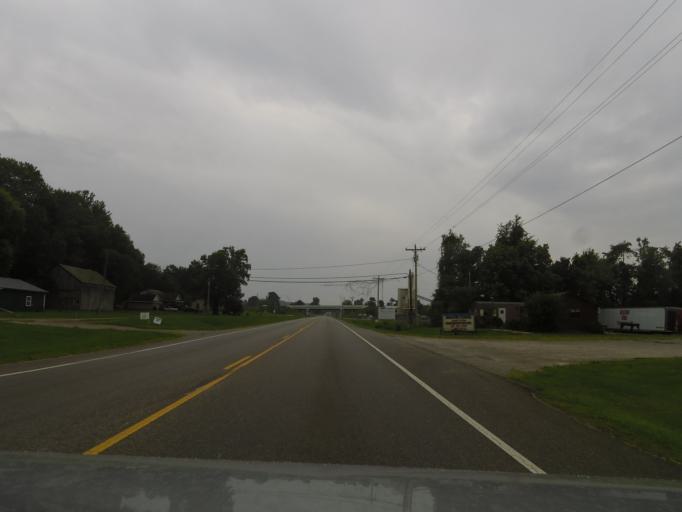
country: US
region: Ohio
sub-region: Brown County
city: Aberdeen
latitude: 38.6895
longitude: -83.7786
